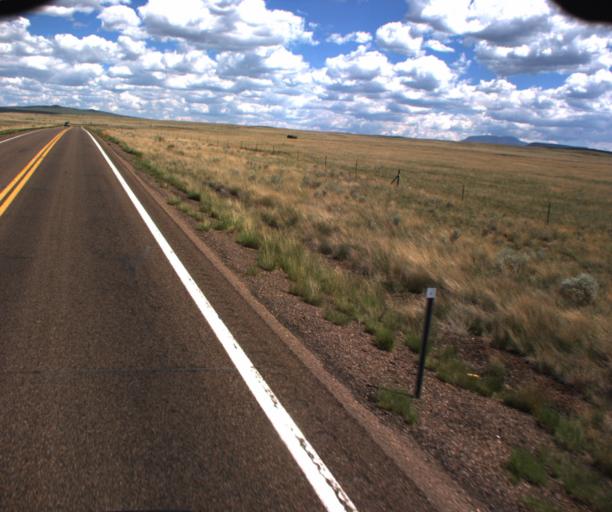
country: US
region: Arizona
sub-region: Apache County
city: Springerville
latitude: 34.1892
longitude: -109.3446
